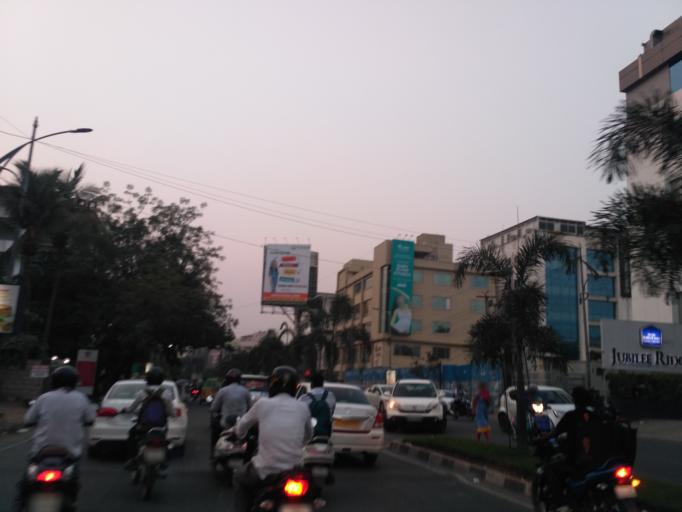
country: IN
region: Telangana
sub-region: Rangareddi
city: Kukatpalli
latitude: 17.4399
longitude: 78.3984
